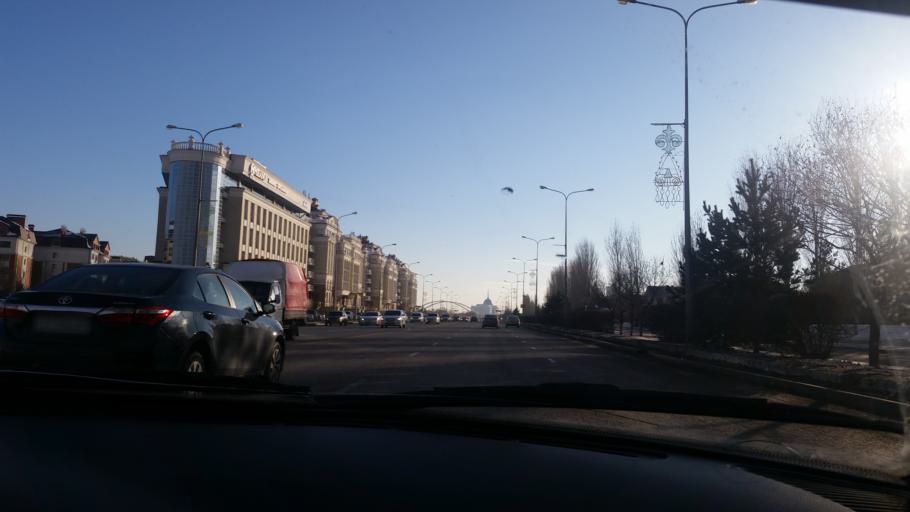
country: KZ
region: Astana Qalasy
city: Astana
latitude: 51.1459
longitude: 71.4448
